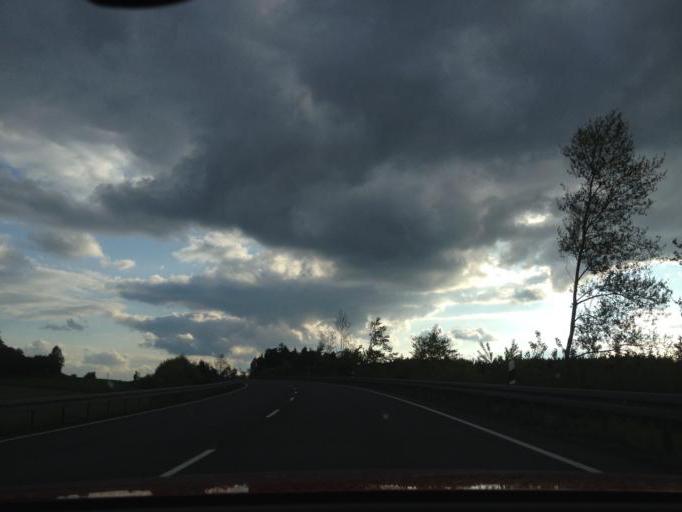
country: DE
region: Bavaria
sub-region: Upper Franconia
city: Marktredwitz
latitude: 50.0233
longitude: 12.1330
